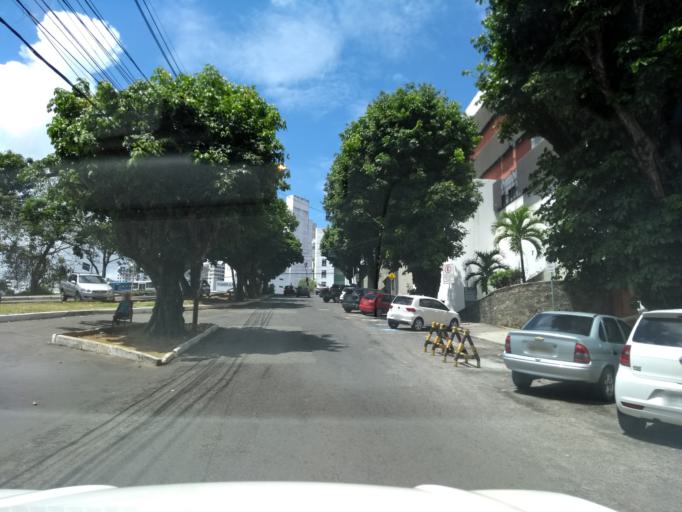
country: BR
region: Bahia
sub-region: Salvador
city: Salvador
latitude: -12.9978
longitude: -38.5162
